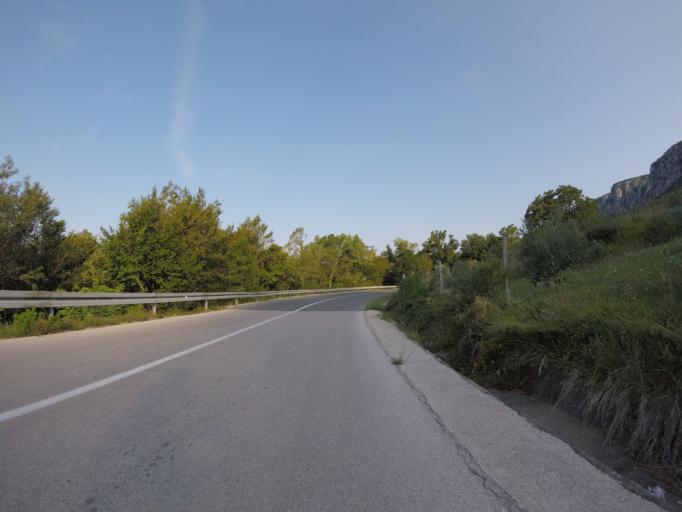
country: HR
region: Primorsko-Goranska
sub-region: Grad Crikvenica
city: Crikvenica
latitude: 45.2057
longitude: 14.7142
